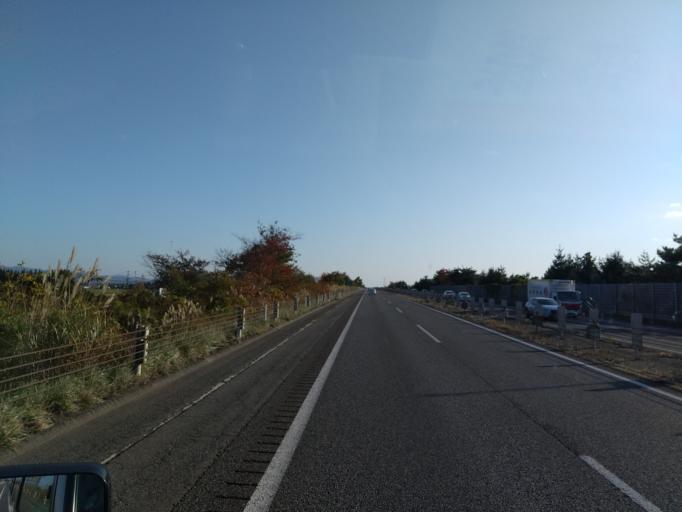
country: JP
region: Iwate
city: Morioka-shi
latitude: 39.6406
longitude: 141.1259
